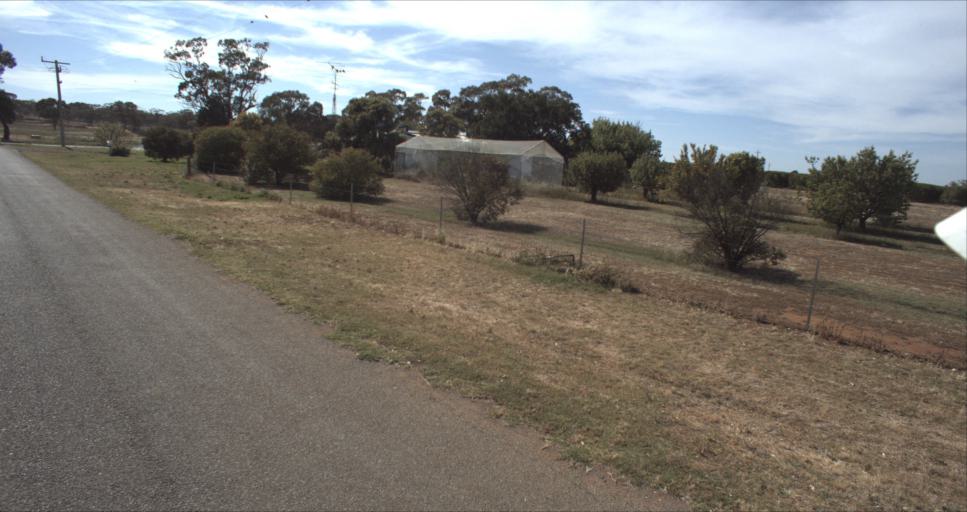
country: AU
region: New South Wales
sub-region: Leeton
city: Leeton
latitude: -34.5869
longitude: 146.4762
